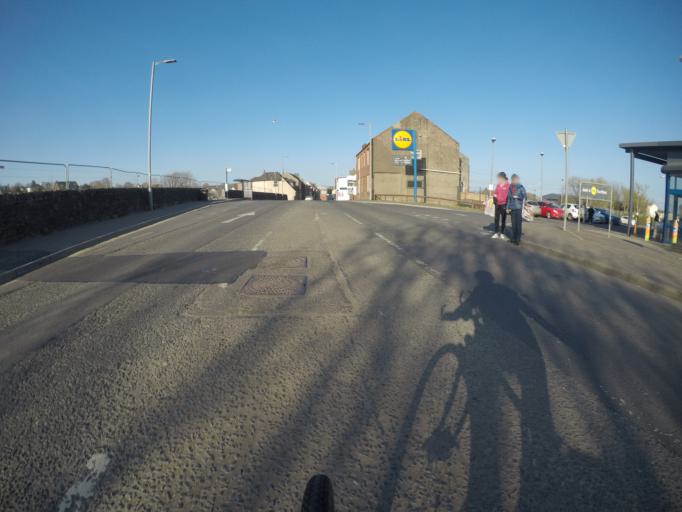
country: GB
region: Scotland
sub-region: North Ayrshire
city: Stevenston
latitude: 55.6390
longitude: -4.7619
